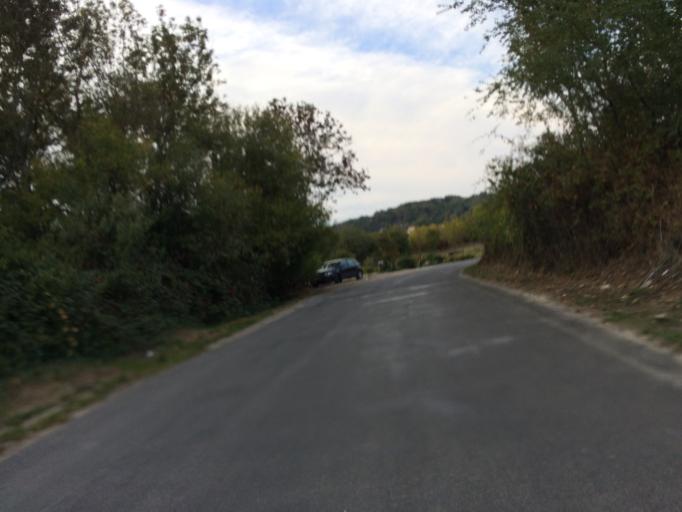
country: FR
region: Ile-de-France
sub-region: Departement de l'Essonne
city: Linas
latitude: 48.6351
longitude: 2.2620
